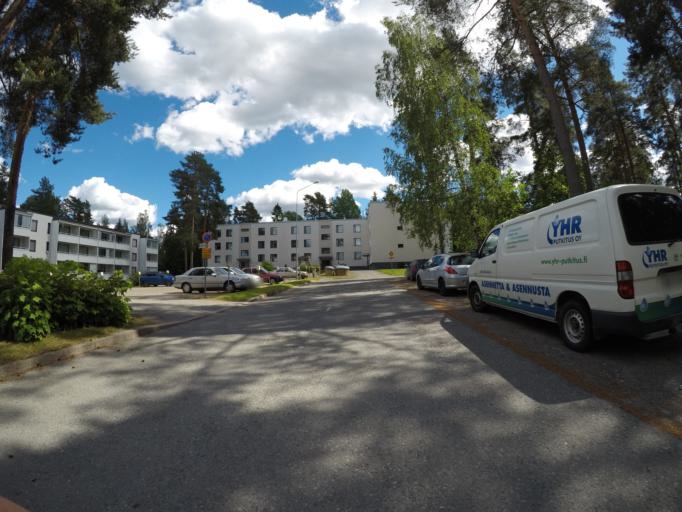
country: FI
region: Haeme
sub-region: Haemeenlinna
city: Haemeenlinna
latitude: 61.0147
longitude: 24.4368
